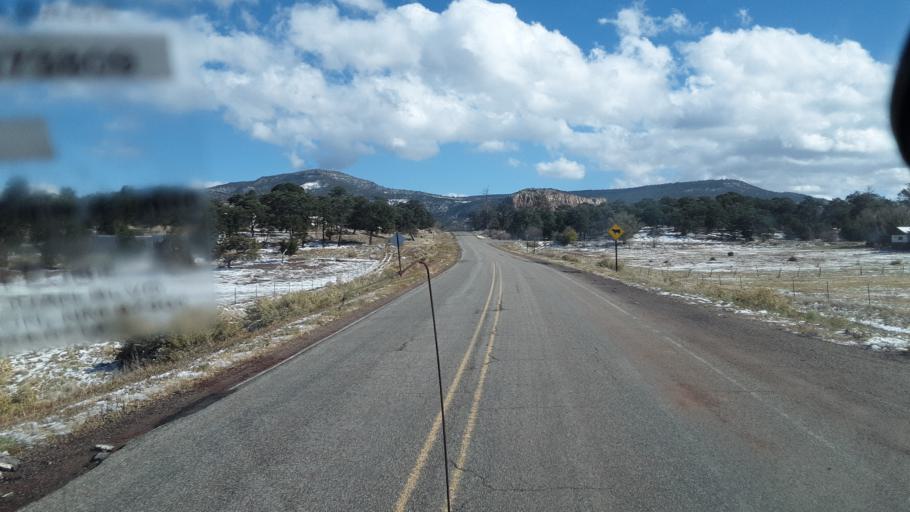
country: US
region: New Mexico
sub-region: Rio Arriba County
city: Santa Teresa
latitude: 36.2283
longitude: -106.8216
